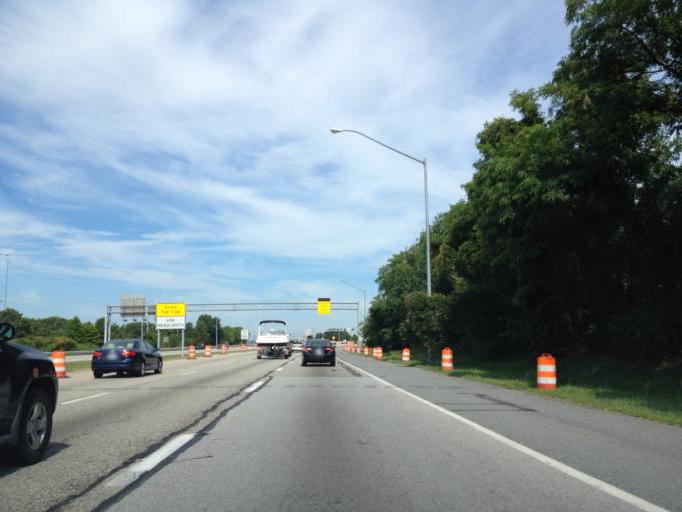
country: US
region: Maryland
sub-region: Queen Anne's County
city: Stevensville
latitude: 38.9811
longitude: -76.3298
